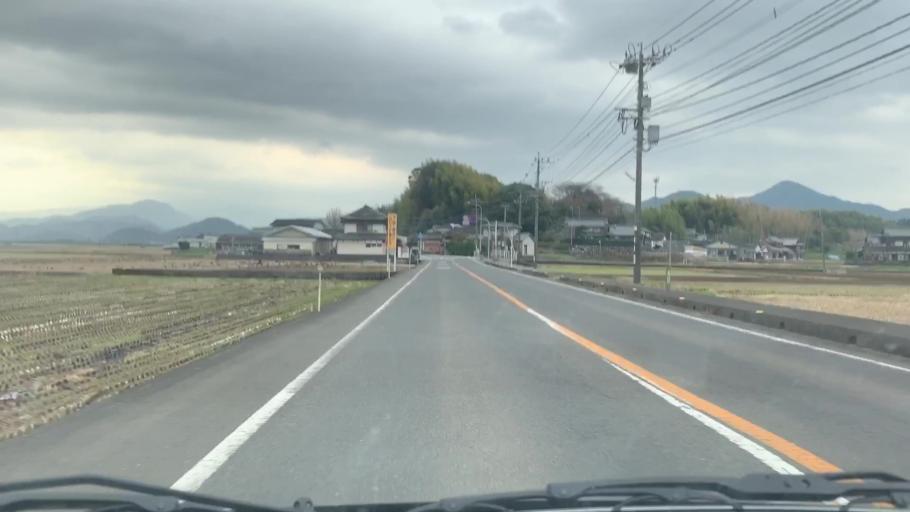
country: JP
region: Saga Prefecture
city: Kashima
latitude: 33.1415
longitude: 130.0639
